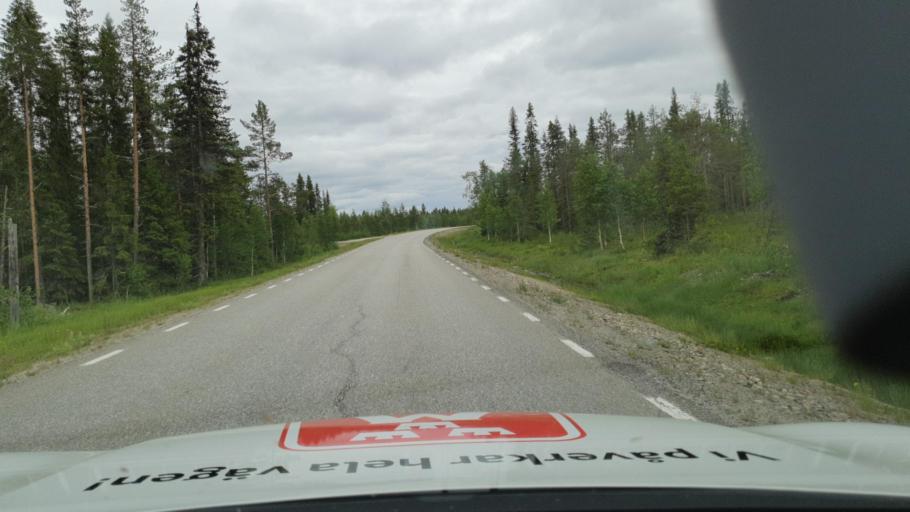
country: SE
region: Vaesterbotten
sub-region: Lycksele Kommun
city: Soderfors
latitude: 64.3023
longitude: 18.1726
